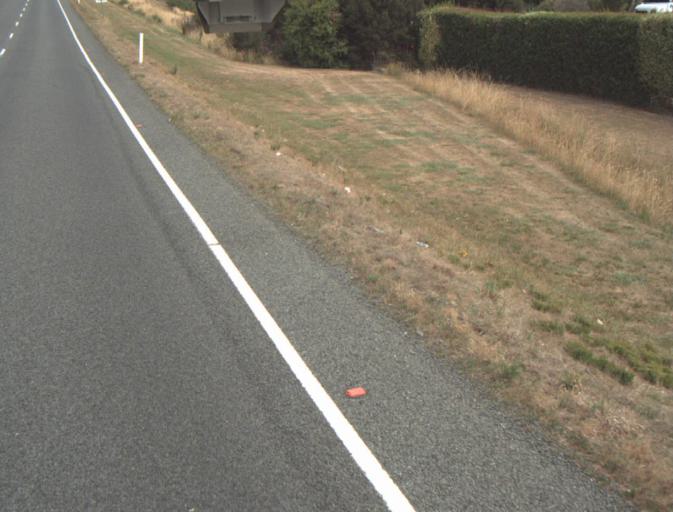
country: AU
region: Tasmania
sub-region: Launceston
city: Mayfield
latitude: -41.2818
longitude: 147.0389
